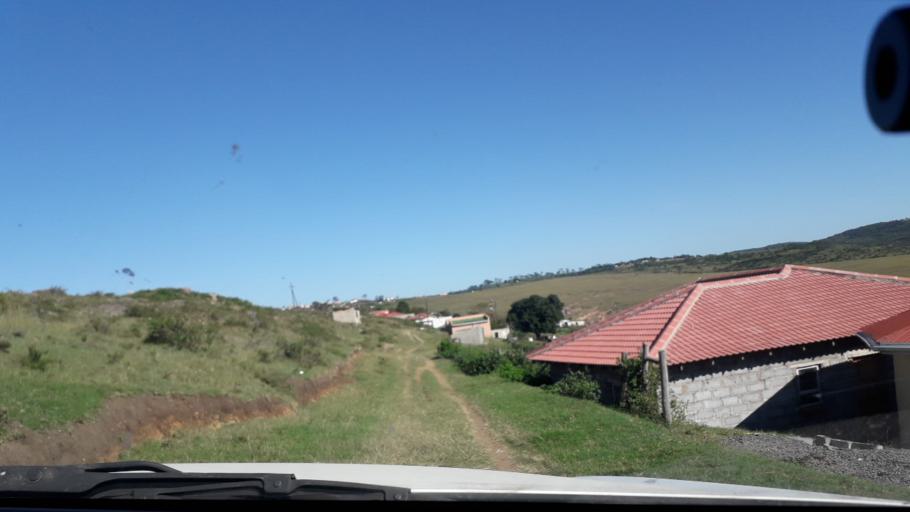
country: ZA
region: Eastern Cape
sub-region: Buffalo City Metropolitan Municipality
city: East London
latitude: -32.8377
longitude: 27.9980
